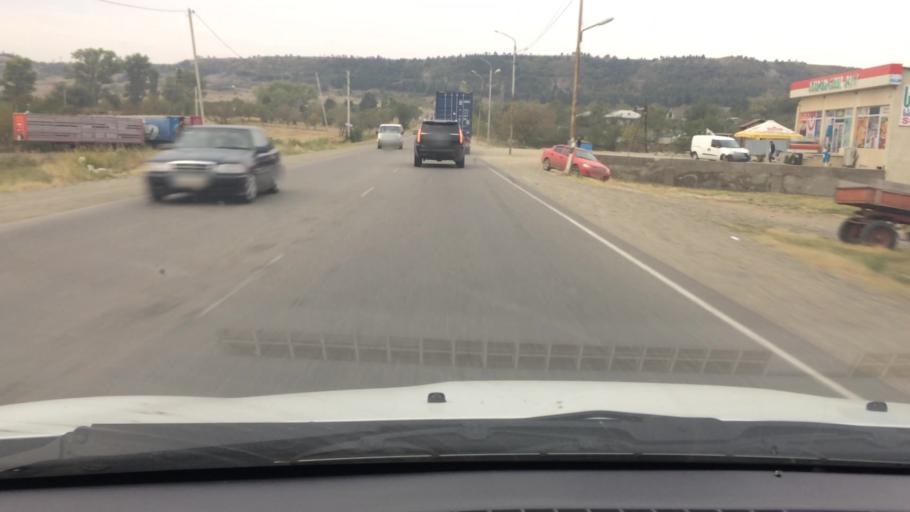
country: GE
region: T'bilisi
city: Tbilisi
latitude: 41.6082
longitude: 44.7844
